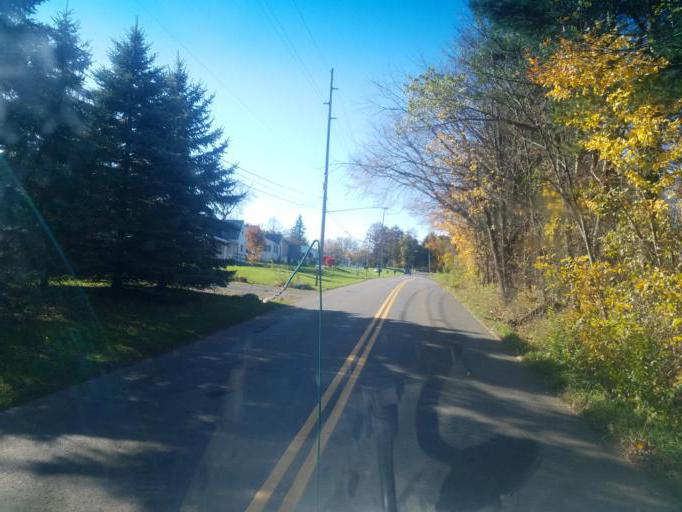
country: US
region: Ohio
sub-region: Richland County
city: Ontario
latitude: 40.7837
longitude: -82.5542
